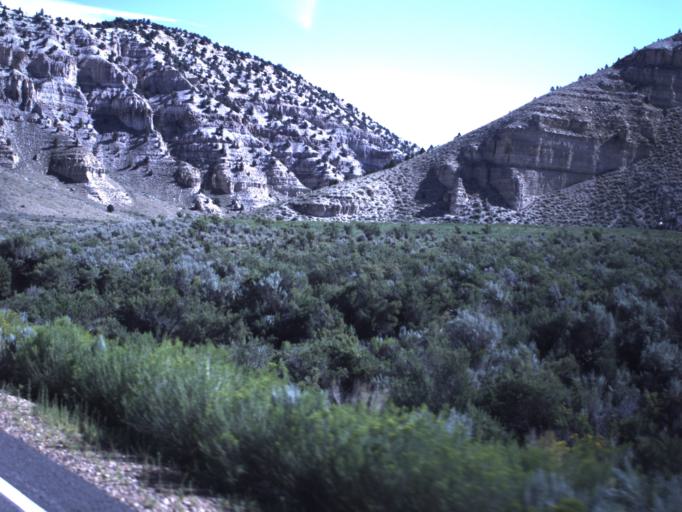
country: US
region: Utah
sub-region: Duchesne County
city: Duchesne
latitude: 40.0417
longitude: -110.5373
